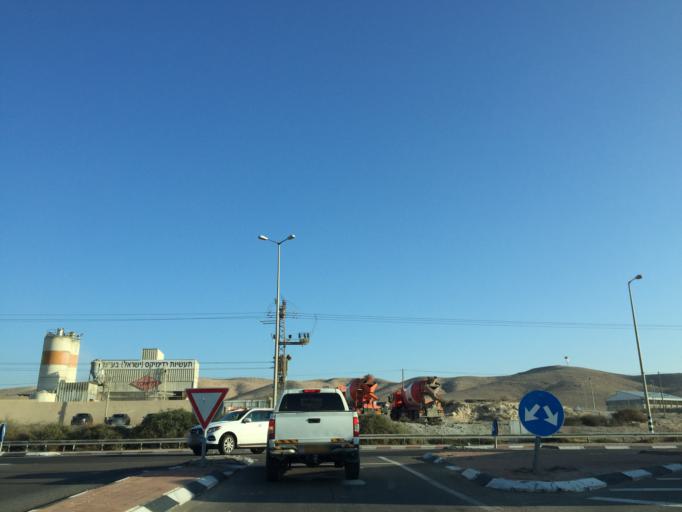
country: IL
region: Southern District
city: Dimona
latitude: 31.0679
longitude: 35.0065
